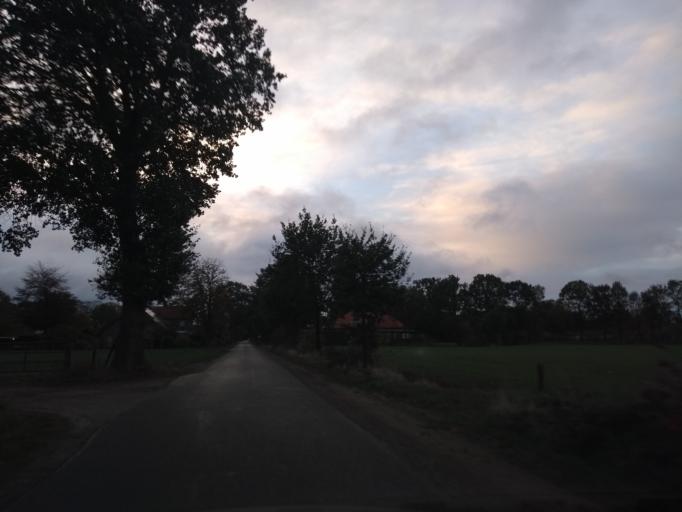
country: NL
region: Gelderland
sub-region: Gemeente Bronckhorst
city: Zelhem
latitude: 52.0133
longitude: 6.3840
